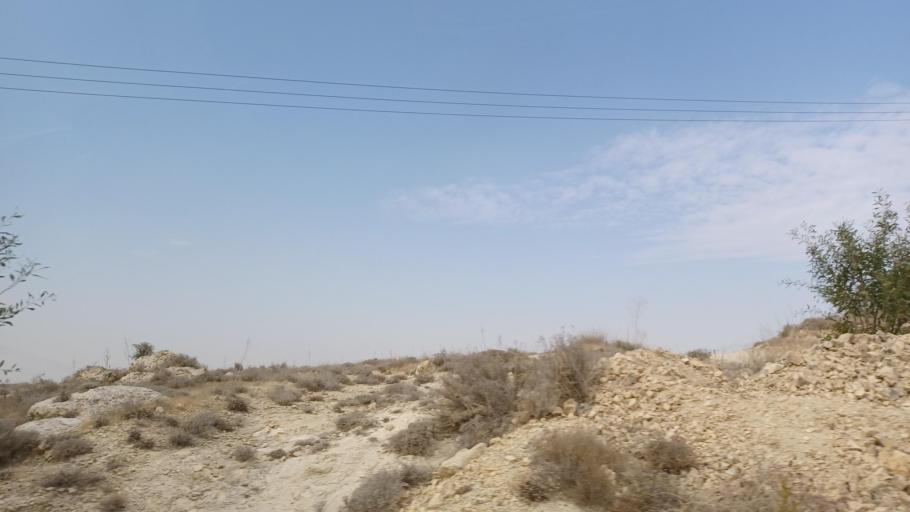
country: CY
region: Lefkosia
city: Meniko
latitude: 35.0642
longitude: 33.1245
